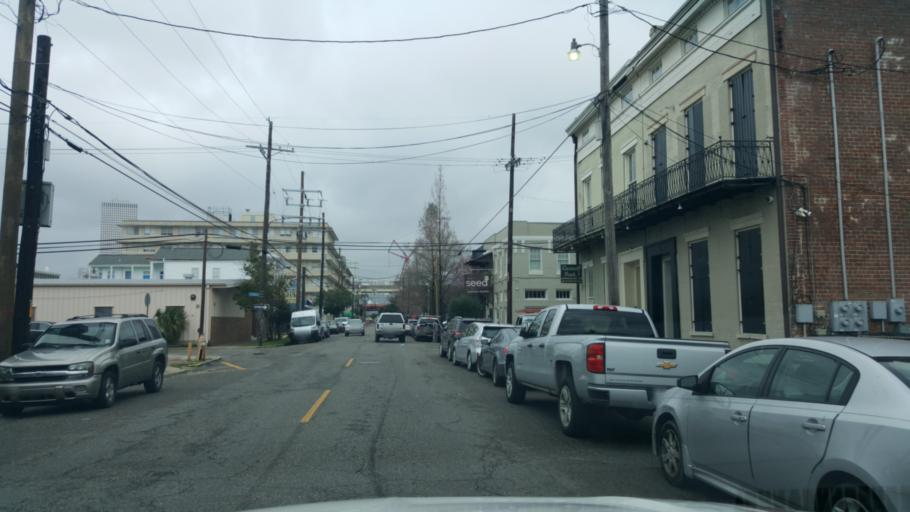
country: US
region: Louisiana
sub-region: Orleans Parish
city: New Orleans
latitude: 29.9387
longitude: -90.0739
